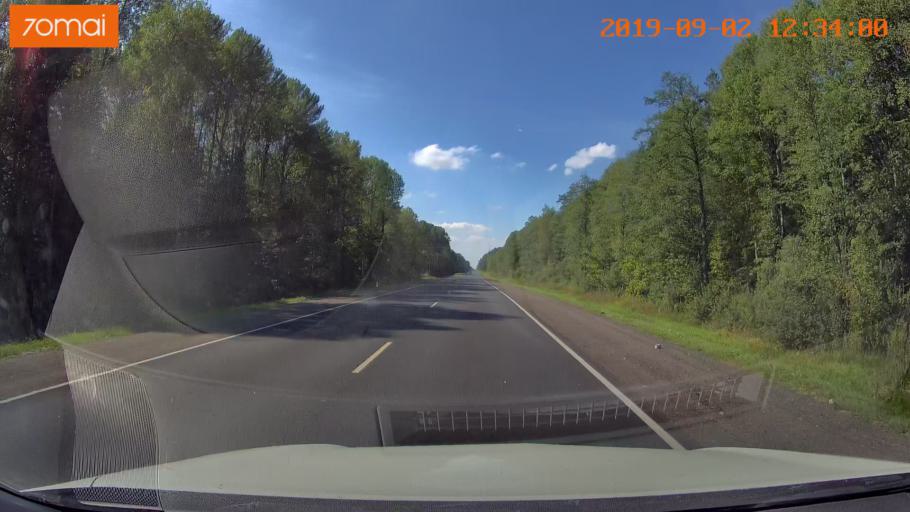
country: RU
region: Smolensk
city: Shumyachi
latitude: 53.8135
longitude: 32.4147
